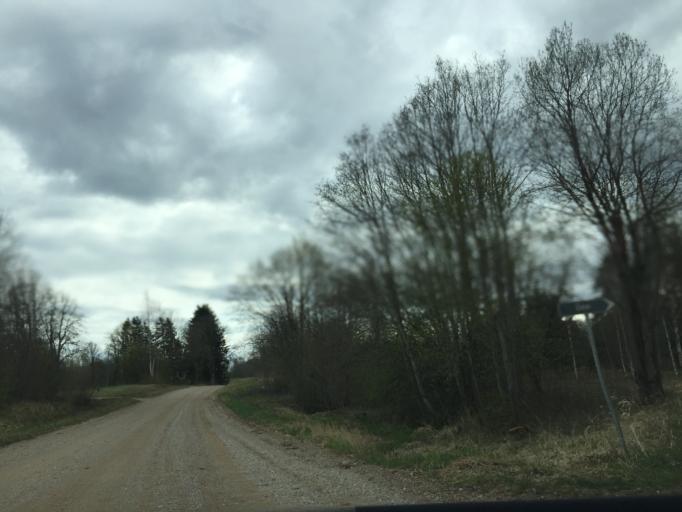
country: LV
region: Jaunpiebalga
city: Jaunpiebalga
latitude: 57.1623
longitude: 26.0711
